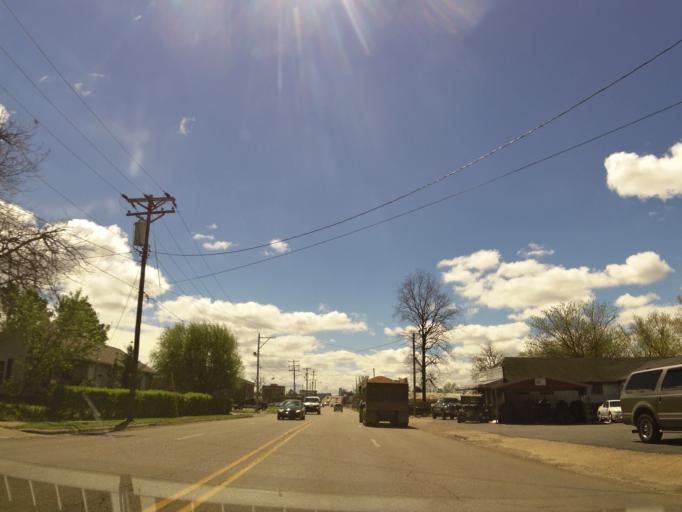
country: US
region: Arkansas
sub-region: Craighead County
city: Jonesboro
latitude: 35.8484
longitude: -90.7046
